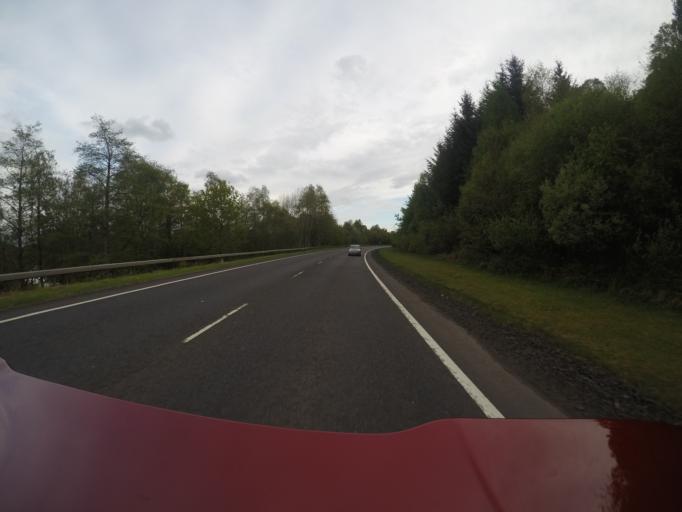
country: GB
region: Scotland
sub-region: West Dunbartonshire
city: Balloch
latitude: 56.1084
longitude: -4.6396
